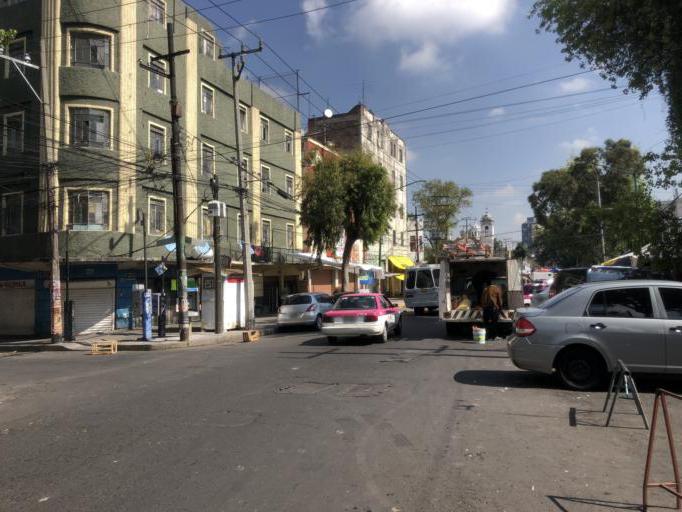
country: MX
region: Mexico City
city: Cuauhtemoc
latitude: 19.4459
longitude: -99.1328
